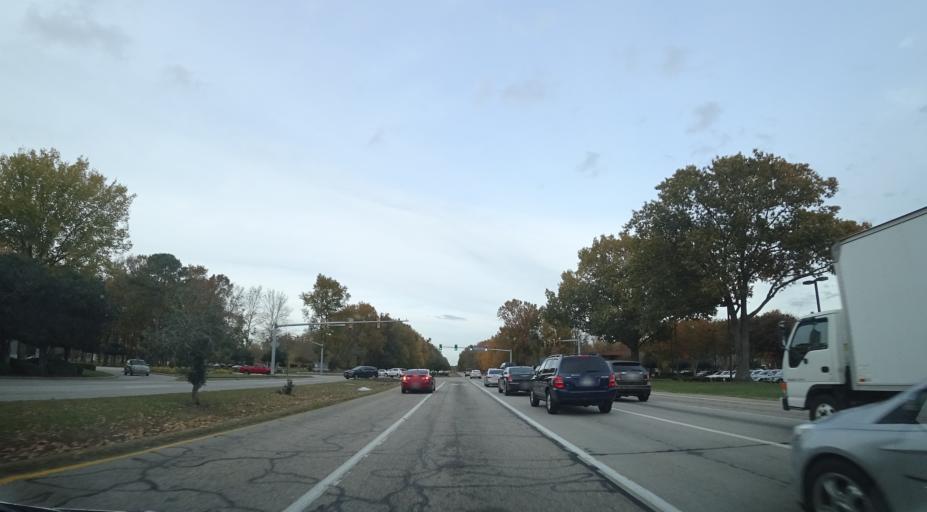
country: US
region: Virginia
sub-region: City of Hampton
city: Hampton
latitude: 37.0628
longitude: -76.4003
